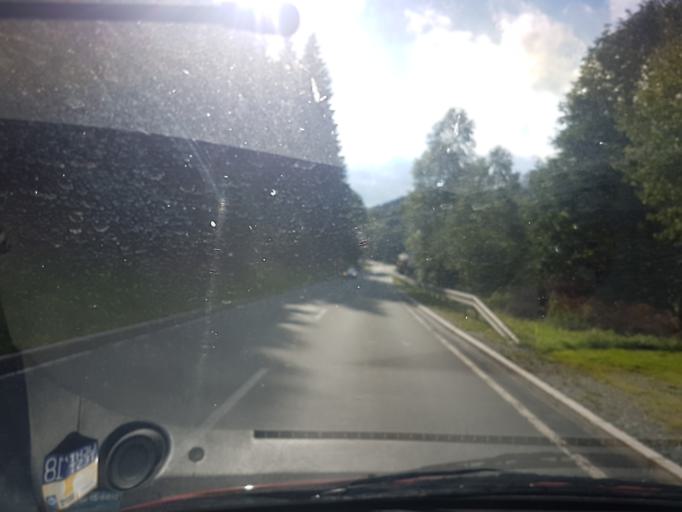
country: DE
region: Bavaria
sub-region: Upper Franconia
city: Warmensteinach
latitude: 50.0058
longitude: 11.8142
